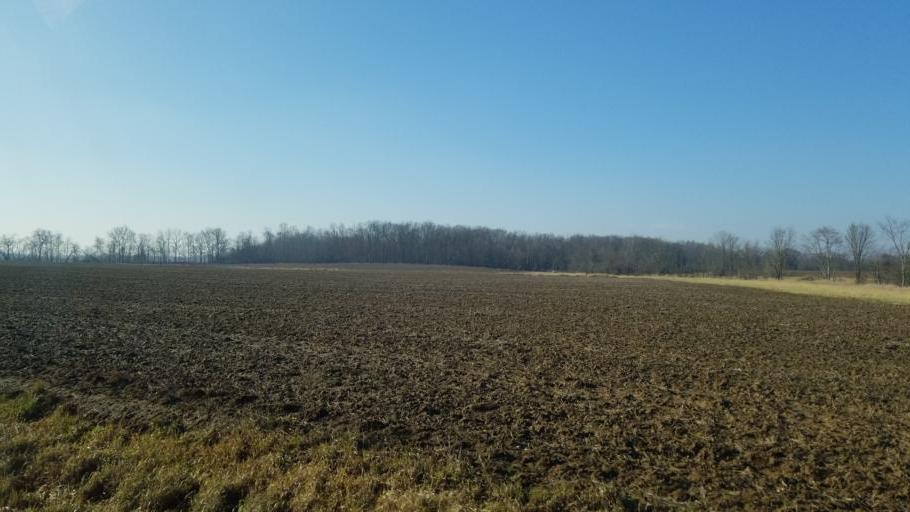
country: US
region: Ohio
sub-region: Seneca County
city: Tiffin
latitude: 41.0913
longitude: -83.1122
